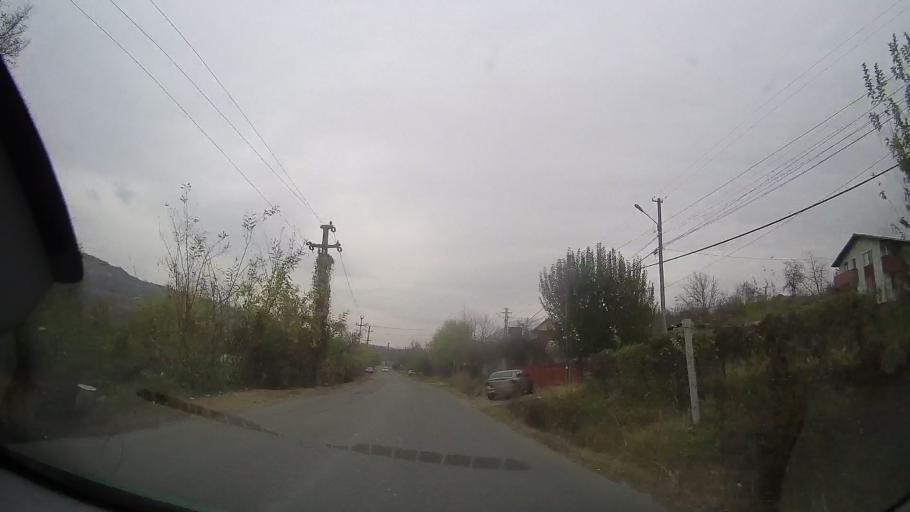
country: RO
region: Prahova
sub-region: Oras Urlati
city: Urlati
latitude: 45.0084
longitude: 26.2281
